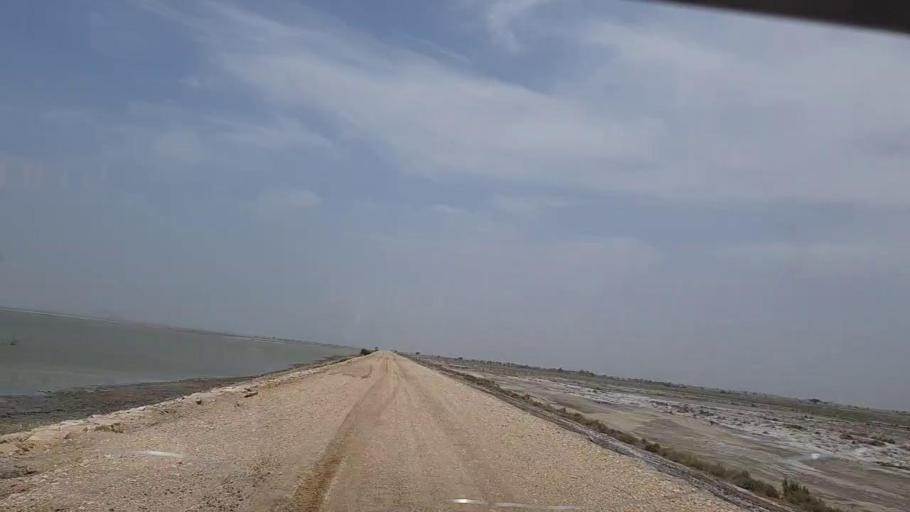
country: PK
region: Sindh
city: Sehwan
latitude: 26.4143
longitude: 67.7678
